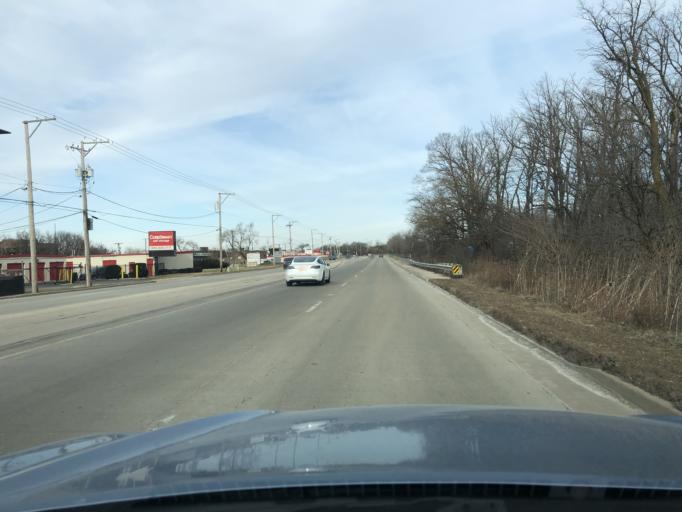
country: US
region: Illinois
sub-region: Cook County
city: Wheeling
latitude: 42.1194
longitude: -87.8952
